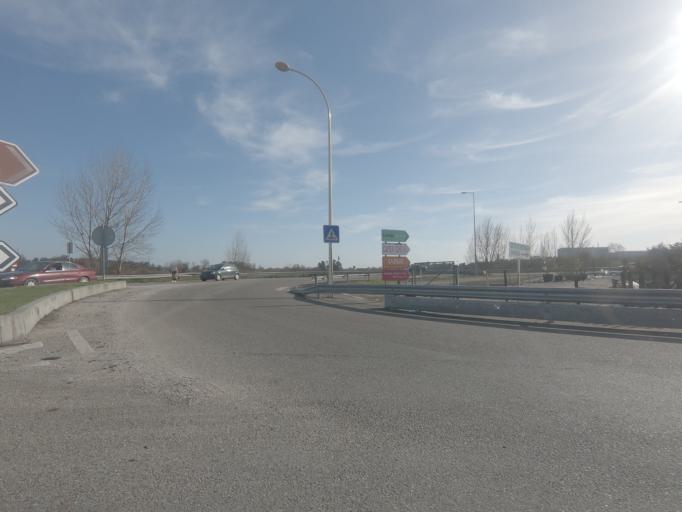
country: PT
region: Santarem
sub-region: Torres Novas
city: Torres Novas
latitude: 39.4640
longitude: -8.5296
